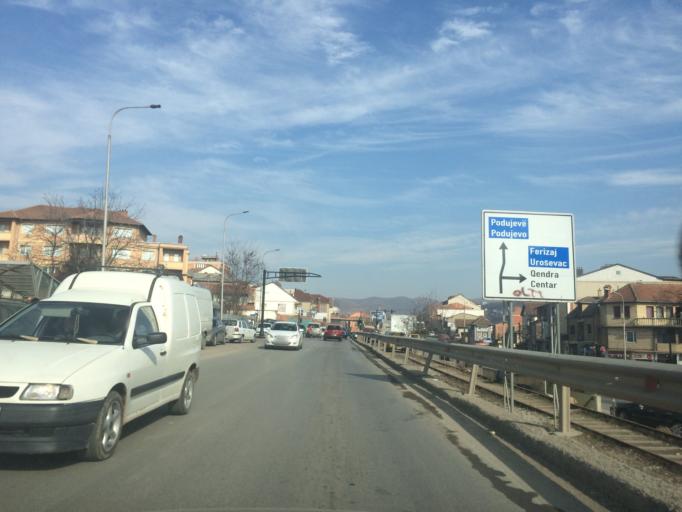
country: XK
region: Pristina
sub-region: Komuna e Prishtines
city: Pristina
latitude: 42.6713
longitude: 21.1611
